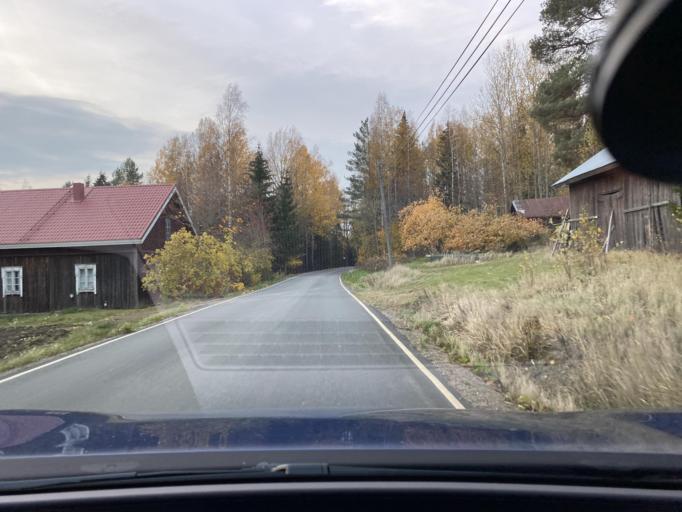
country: FI
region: Varsinais-Suomi
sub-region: Loimaa
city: Alastaro
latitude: 61.0986
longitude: 22.8950
